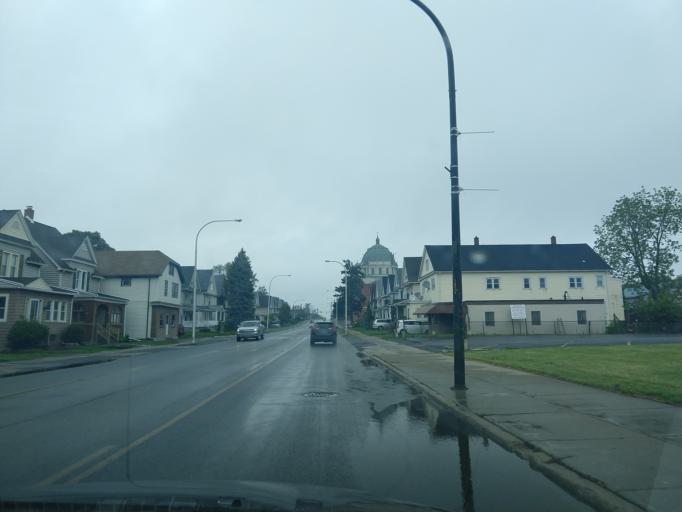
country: US
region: New York
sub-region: Erie County
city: Lackawanna
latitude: 42.8226
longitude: -78.8240
